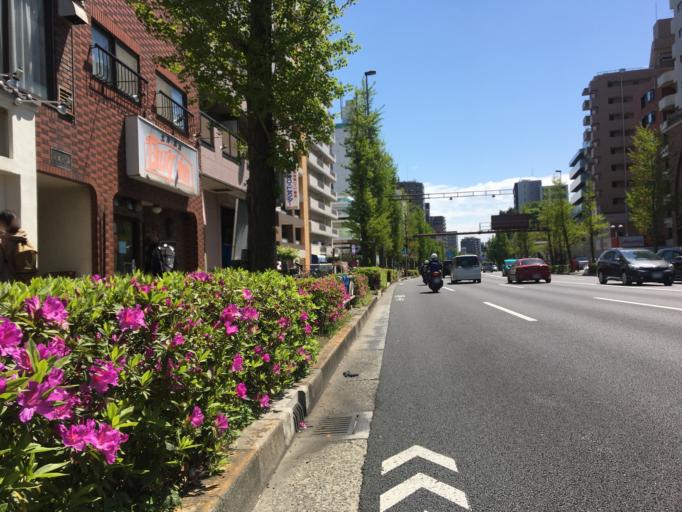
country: JP
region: Saitama
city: Kawaguchi
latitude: 35.7748
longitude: 139.6966
